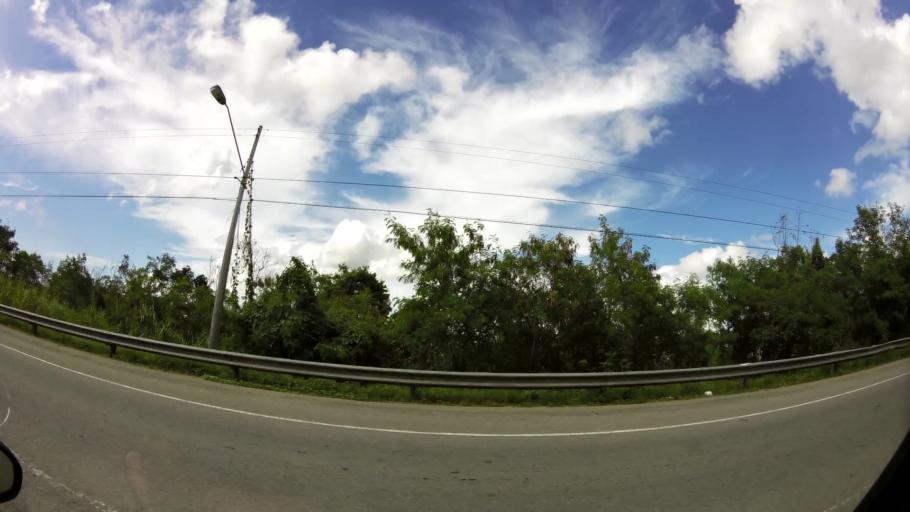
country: TT
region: City of San Fernando
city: Mon Repos
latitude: 10.2620
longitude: -61.4510
